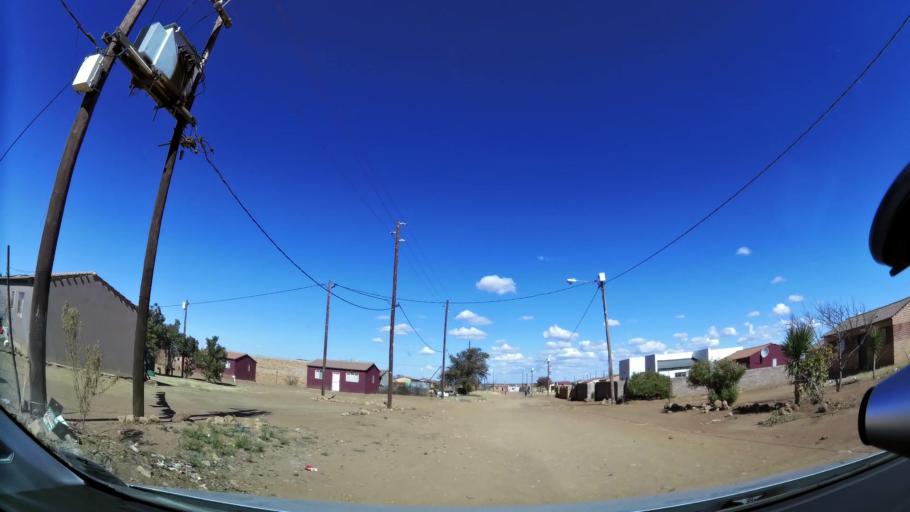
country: ZA
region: North-West
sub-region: Dr Kenneth Kaunda District Municipality
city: Klerksdorp
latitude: -26.8669
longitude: 26.5682
